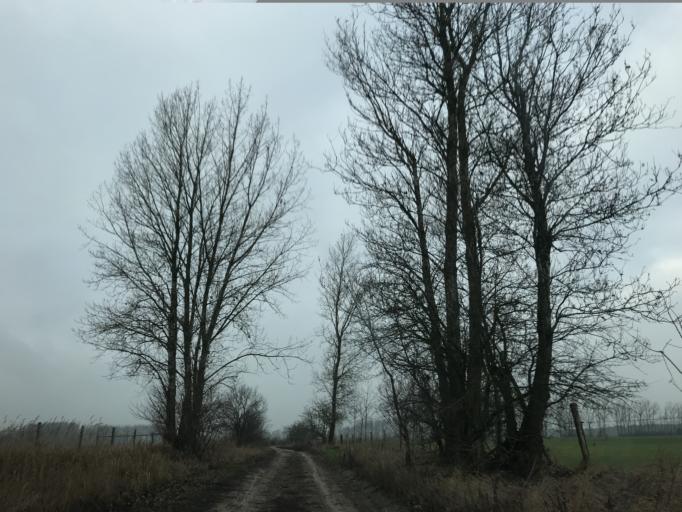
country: DE
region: Brandenburg
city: Kremmen
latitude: 52.7392
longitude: 12.9796
